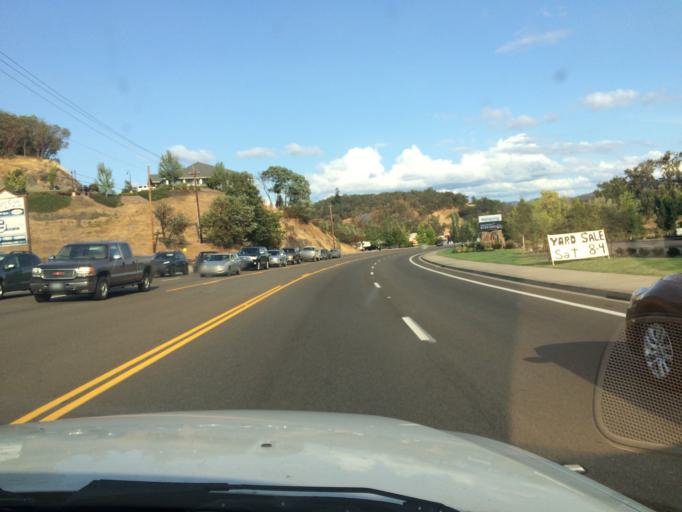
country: US
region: Oregon
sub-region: Douglas County
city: Roseburg
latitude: 43.2349
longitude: -123.3789
